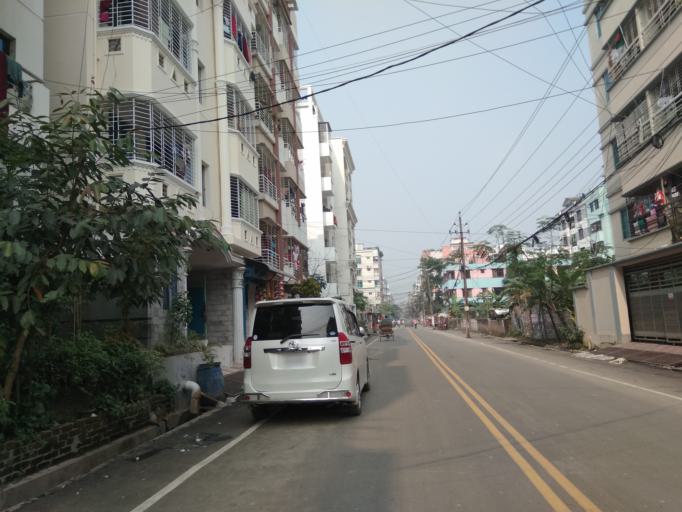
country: BD
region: Dhaka
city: Tungi
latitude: 23.8680
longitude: 90.3833
